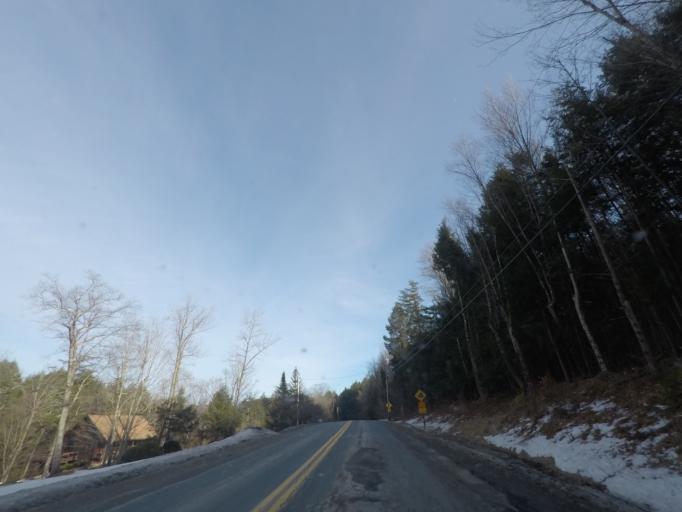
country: US
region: New York
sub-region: Rensselaer County
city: Hoosick Falls
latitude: 42.7349
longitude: -73.3730
